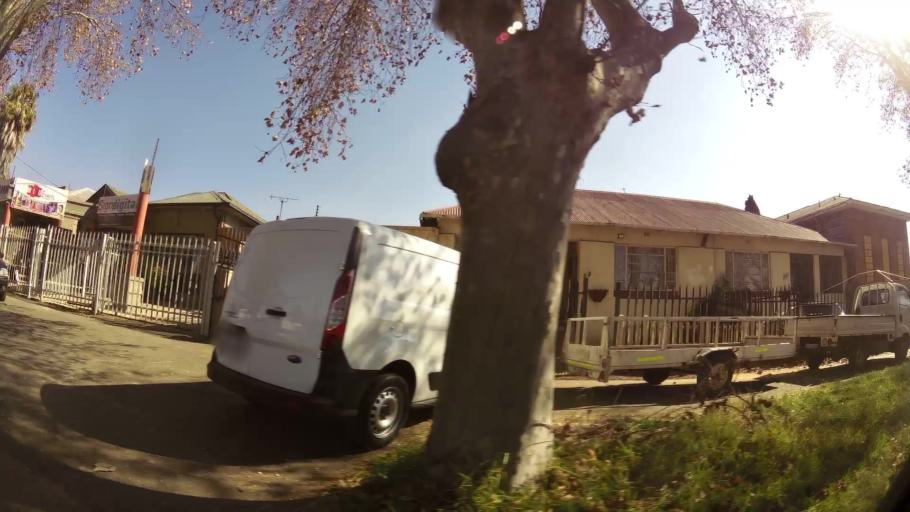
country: ZA
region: Gauteng
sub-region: City of Johannesburg Metropolitan Municipality
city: Johannesburg
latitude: -26.2533
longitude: 28.0552
